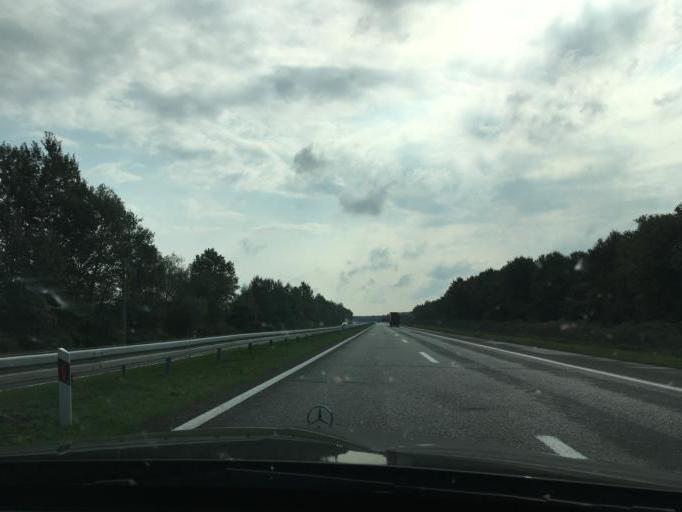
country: HR
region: Brodsko-Posavska
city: Garcin
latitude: 45.1655
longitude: 18.1712
